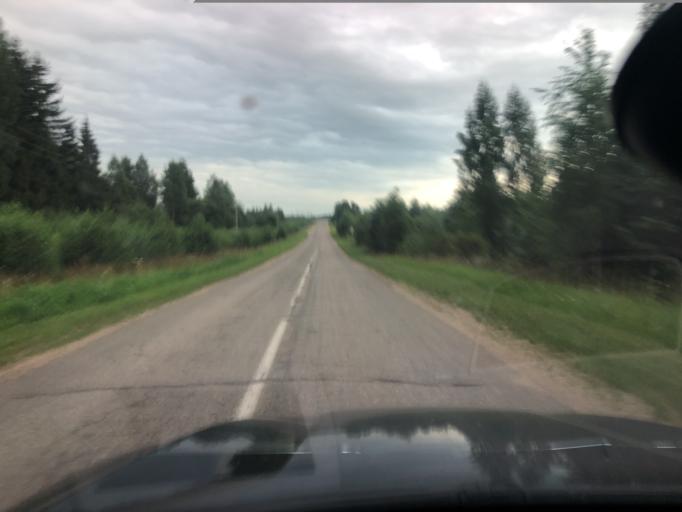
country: RU
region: Jaroslavl
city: Pereslavl'-Zalesskiy
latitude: 57.0245
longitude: 38.9357
